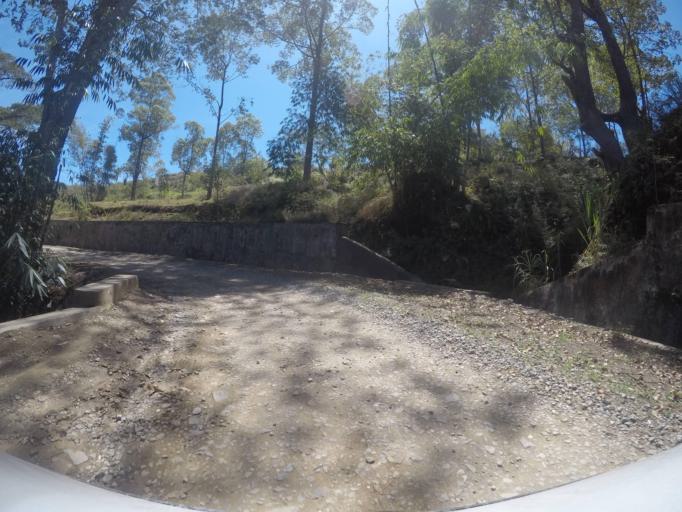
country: TL
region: Ermera
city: Gleno
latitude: -8.7838
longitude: 125.3748
